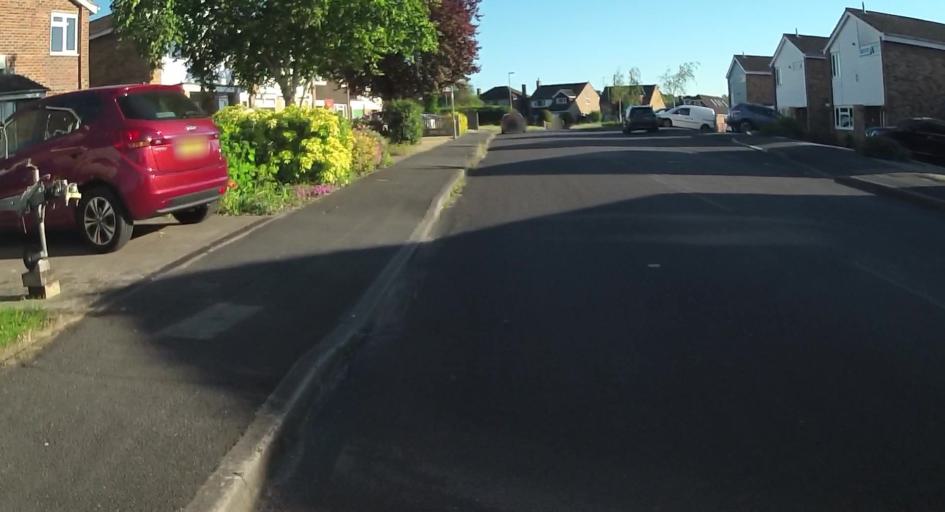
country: GB
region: England
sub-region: Hampshire
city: Basingstoke
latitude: 51.2451
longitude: -1.1339
